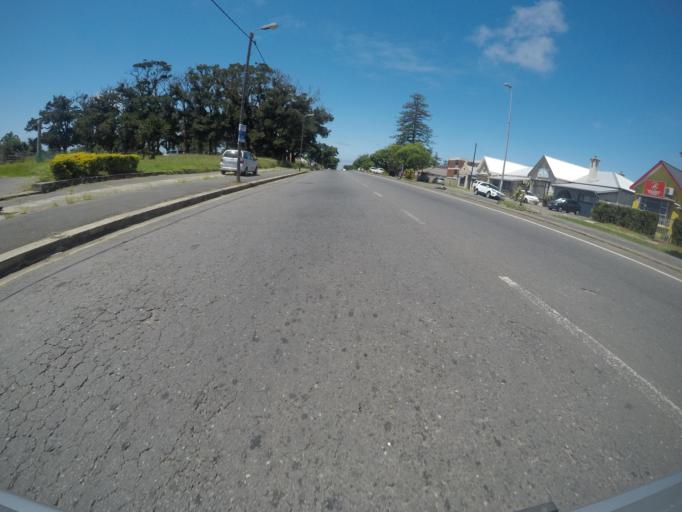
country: ZA
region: Eastern Cape
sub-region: Buffalo City Metropolitan Municipality
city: East London
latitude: -32.9976
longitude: 27.8977
